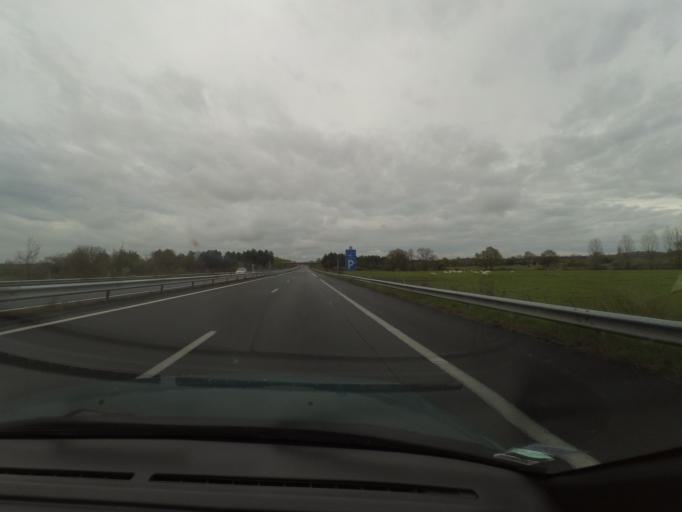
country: FR
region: Pays de la Loire
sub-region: Departement de Maine-et-Loire
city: Seiches-sur-le-Loir
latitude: 47.6138
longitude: -0.2933
